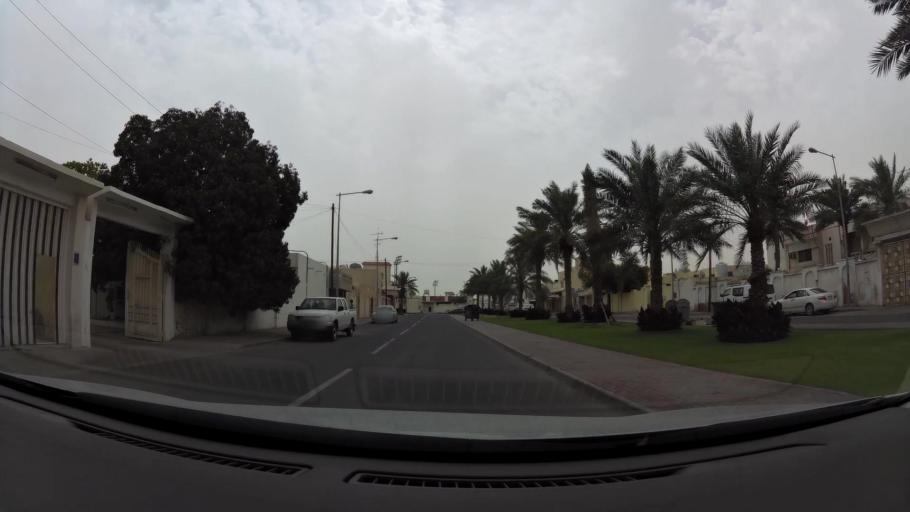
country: QA
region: Baladiyat ad Dawhah
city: Doha
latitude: 25.2623
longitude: 51.5161
